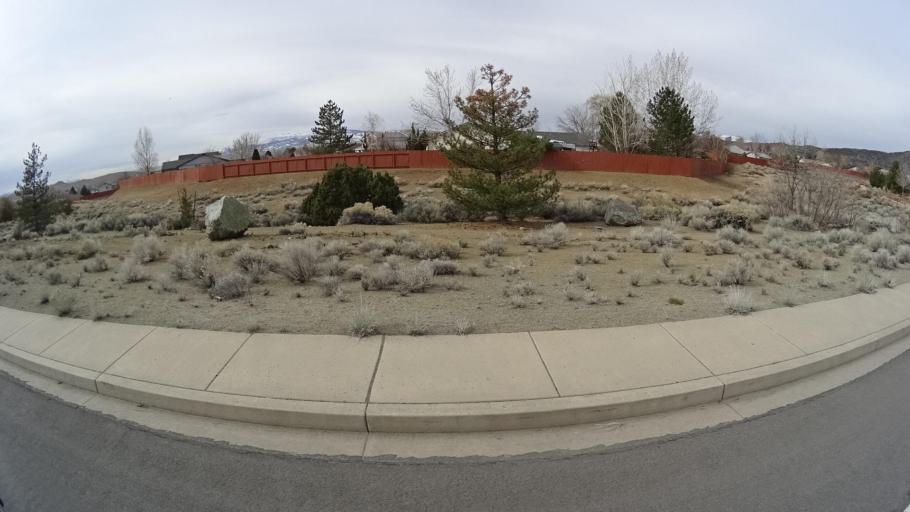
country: US
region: Nevada
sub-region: Washoe County
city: Sun Valley
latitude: 39.6153
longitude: -119.7655
